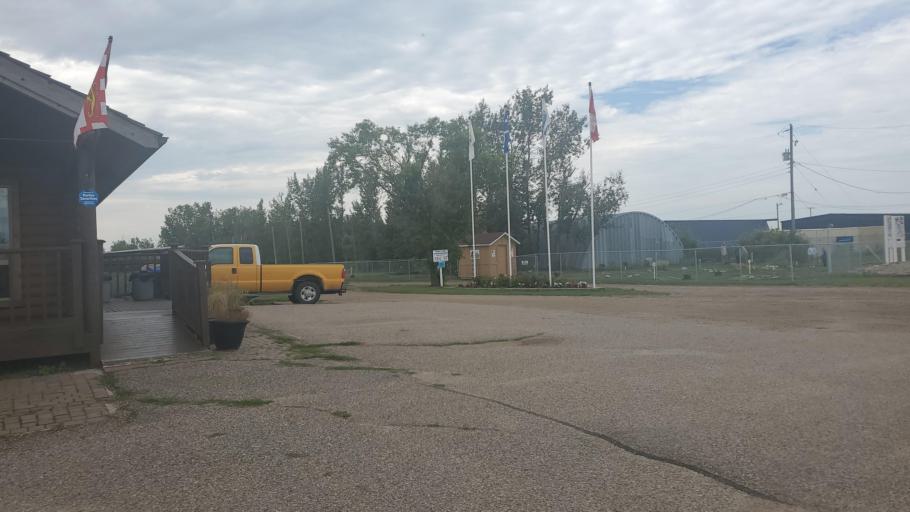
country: CA
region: Saskatchewan
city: Foam Lake
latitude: 51.6373
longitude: -103.5373
